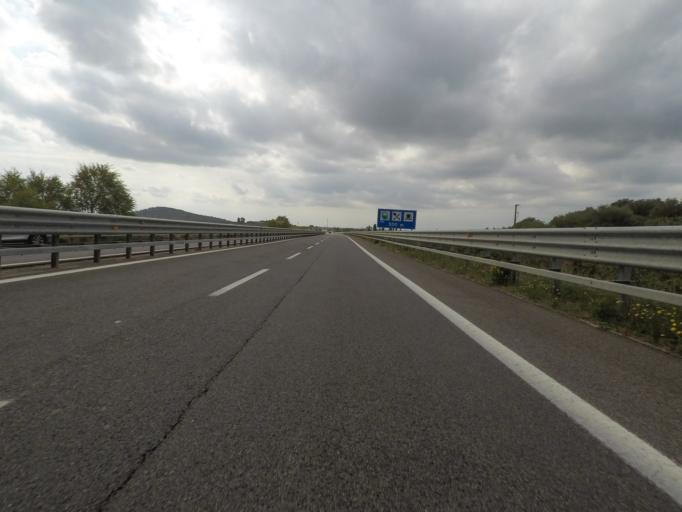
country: IT
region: Tuscany
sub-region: Provincia di Grosseto
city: Bagno Roselle
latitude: 42.8328
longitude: 11.1435
